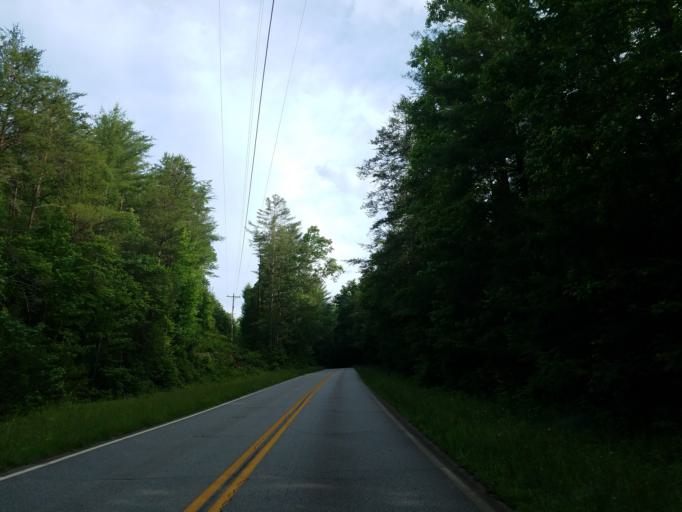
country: US
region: Georgia
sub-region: Lumpkin County
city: Dahlonega
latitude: 34.6194
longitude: -84.0742
